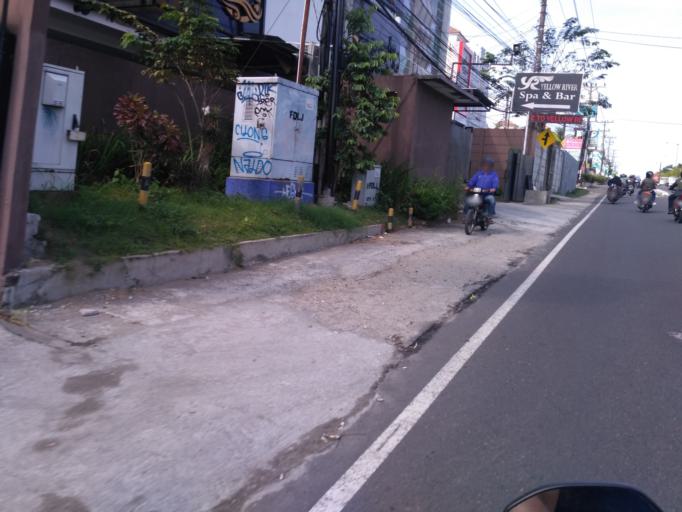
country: ID
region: Daerah Istimewa Yogyakarta
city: Depok
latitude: -7.7629
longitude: 110.4176
